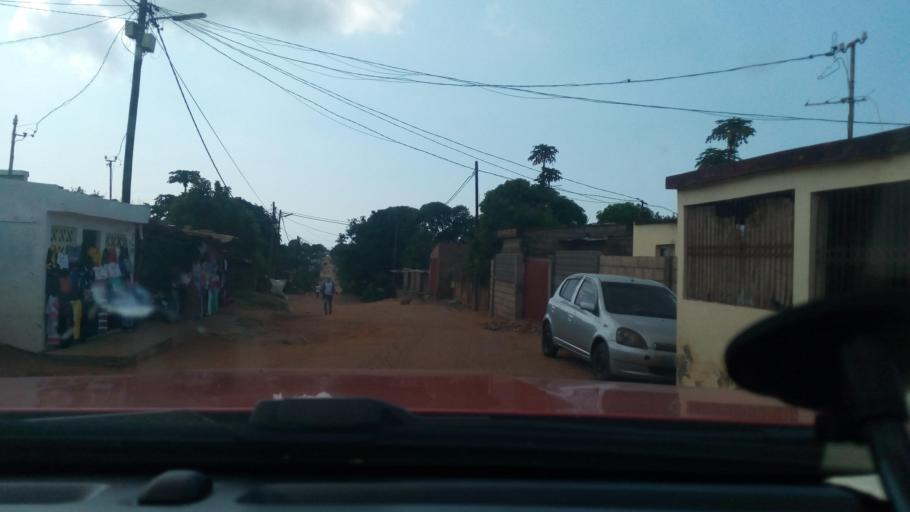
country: MZ
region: Maputo City
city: Maputo
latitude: -25.9214
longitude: 32.5949
